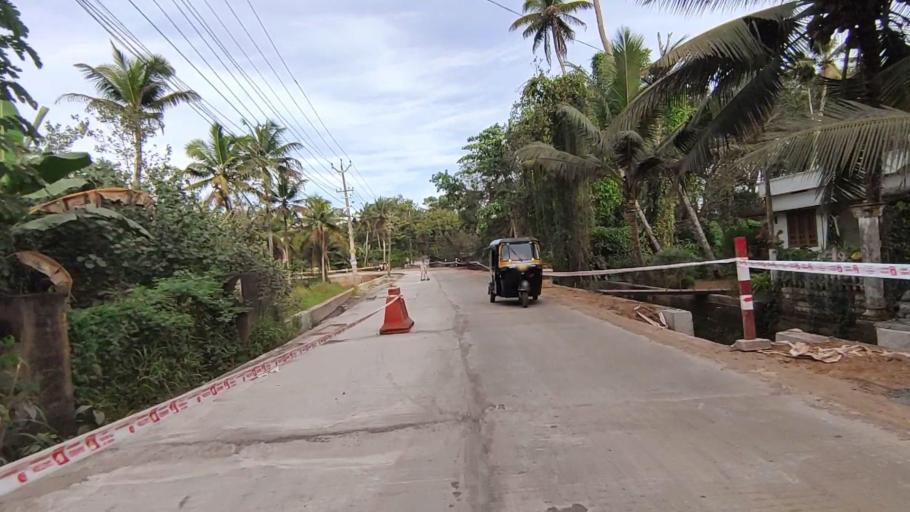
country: IN
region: Kerala
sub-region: Kottayam
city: Kottayam
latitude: 9.6083
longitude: 76.4895
